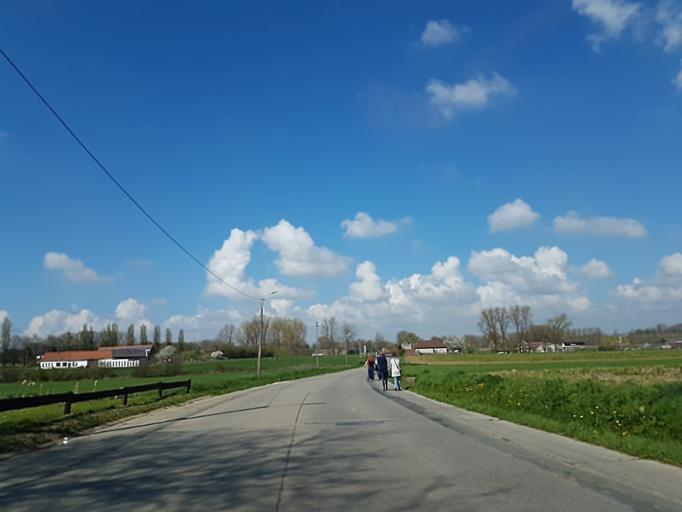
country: BE
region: Flanders
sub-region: Provincie Oost-Vlaanderen
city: Sint-Maria-Lierde
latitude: 50.8186
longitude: 3.8225
